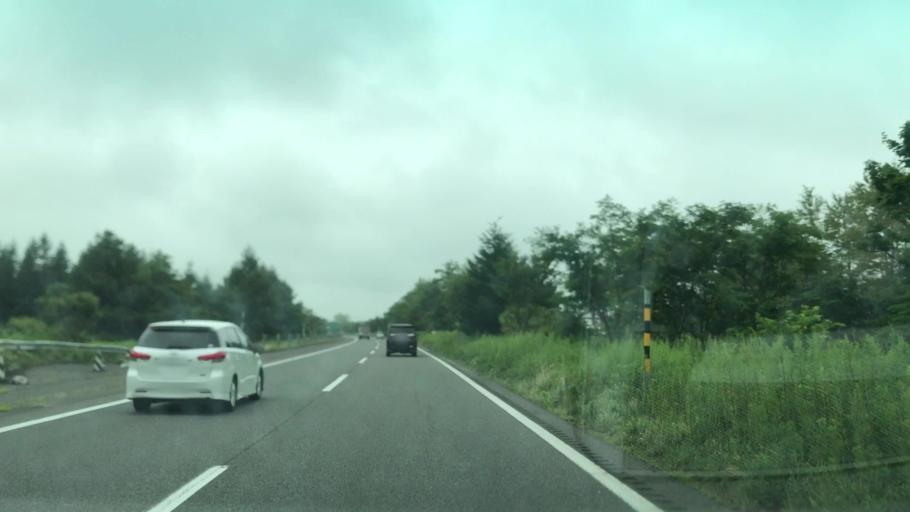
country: JP
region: Hokkaido
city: Chitose
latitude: 42.7864
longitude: 141.6263
